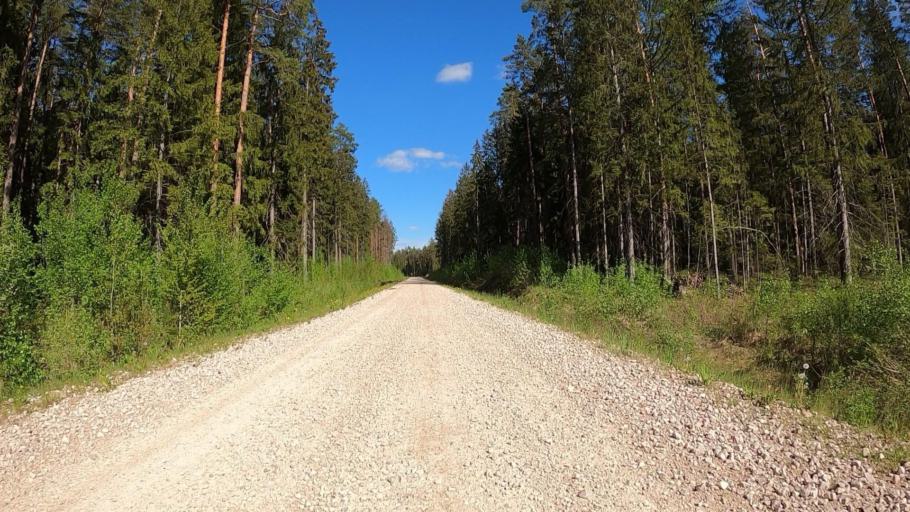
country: LV
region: Baldone
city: Baldone
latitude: 56.7821
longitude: 24.3506
